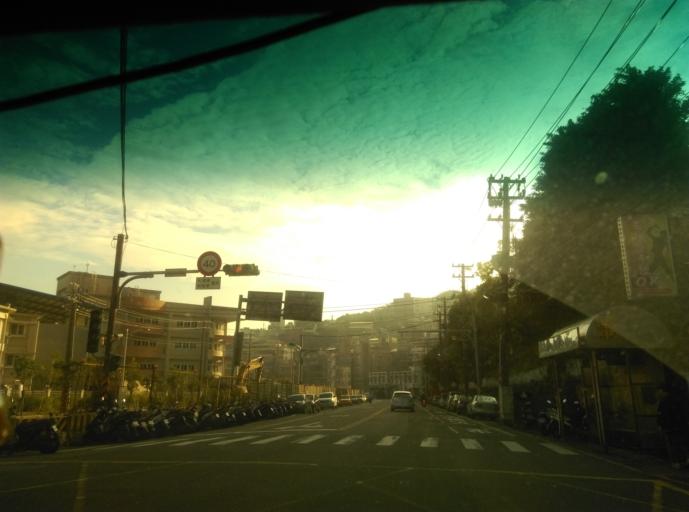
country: TW
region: Taiwan
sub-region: Keelung
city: Keelung
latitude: 25.1446
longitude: 121.7387
